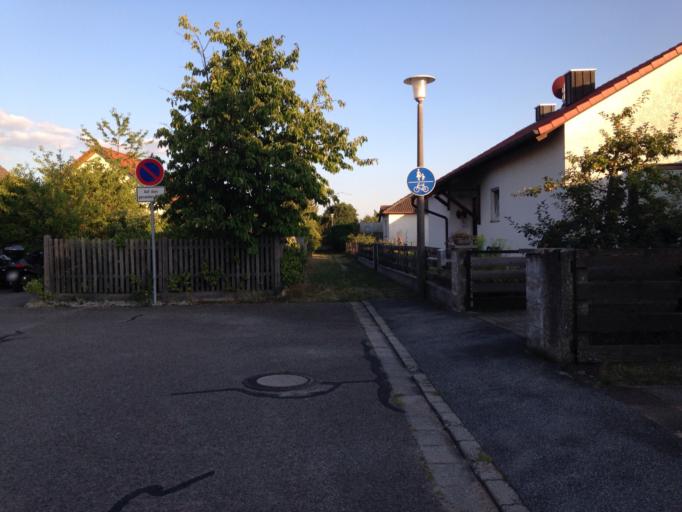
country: DE
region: Bavaria
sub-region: Regierungsbezirk Mittelfranken
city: Hilpoltstein
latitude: 49.1607
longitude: 11.1729
